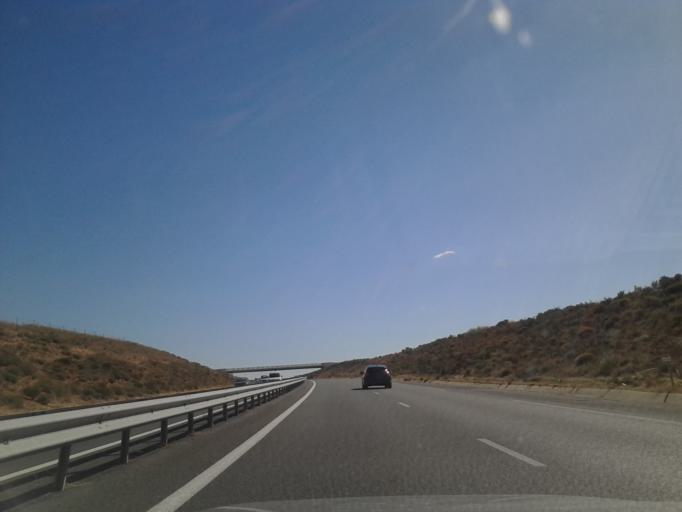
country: FR
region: Languedoc-Roussillon
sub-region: Departement de l'Herault
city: Valros
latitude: 43.4133
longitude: 3.3777
